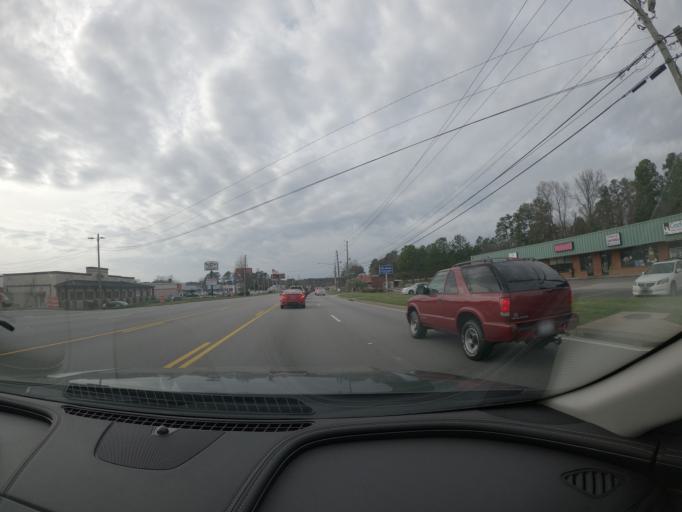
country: US
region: Georgia
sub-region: Columbia County
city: Martinez
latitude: 33.5106
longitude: -82.1031
